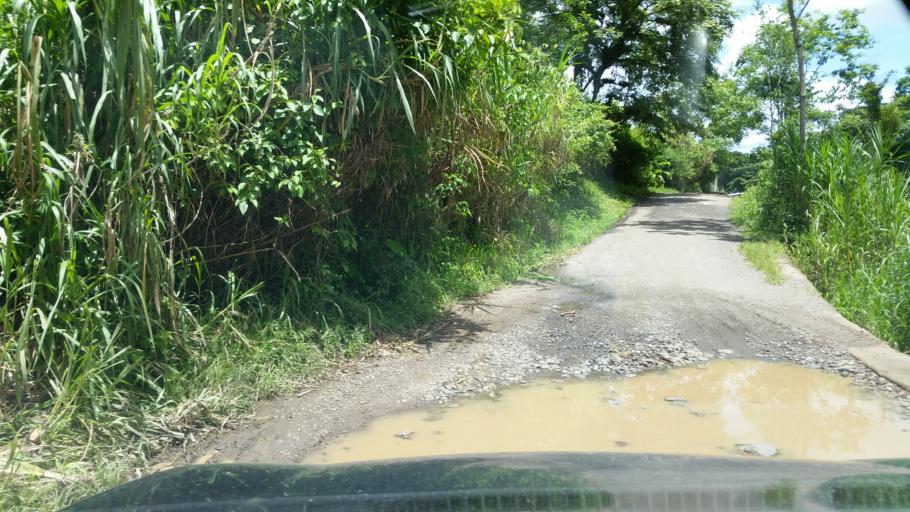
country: NI
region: Atlantico Norte (RAAN)
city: Waslala
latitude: 13.2543
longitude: -85.6179
